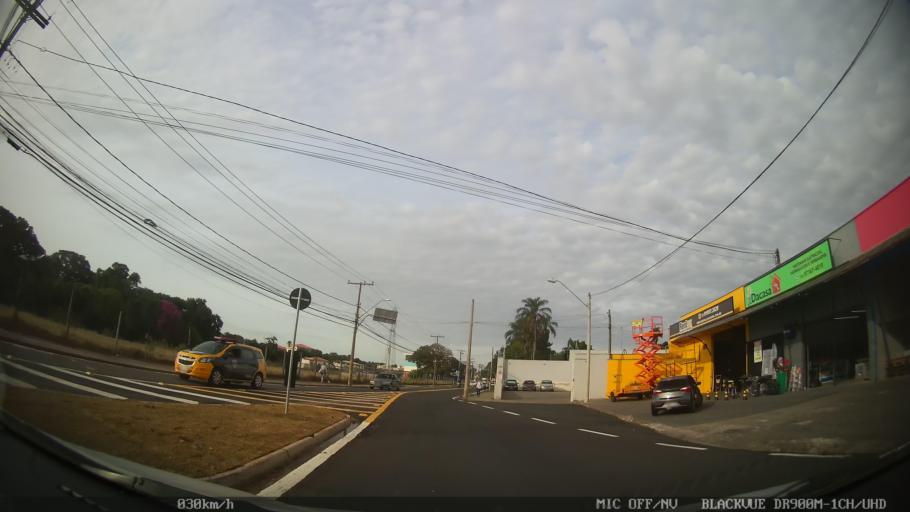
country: BR
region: Sao Paulo
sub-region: Piracicaba
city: Piracicaba
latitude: -22.7424
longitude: -47.6147
